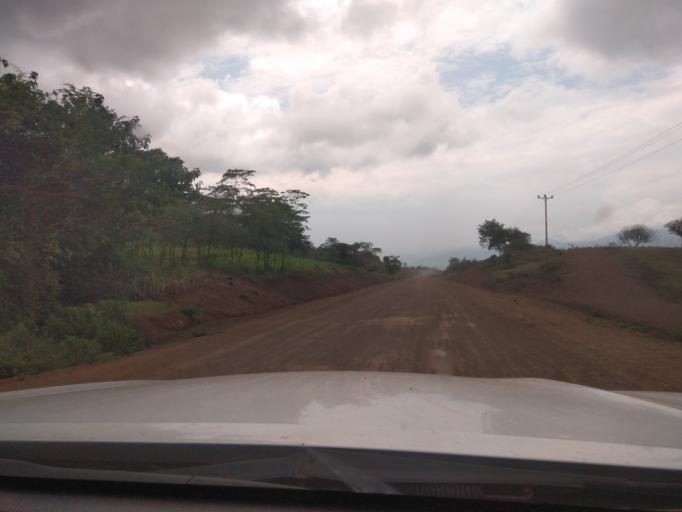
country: ET
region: Southern Nations, Nationalities, and People's Region
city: Felege Neway
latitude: 6.3934
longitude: 37.0720
